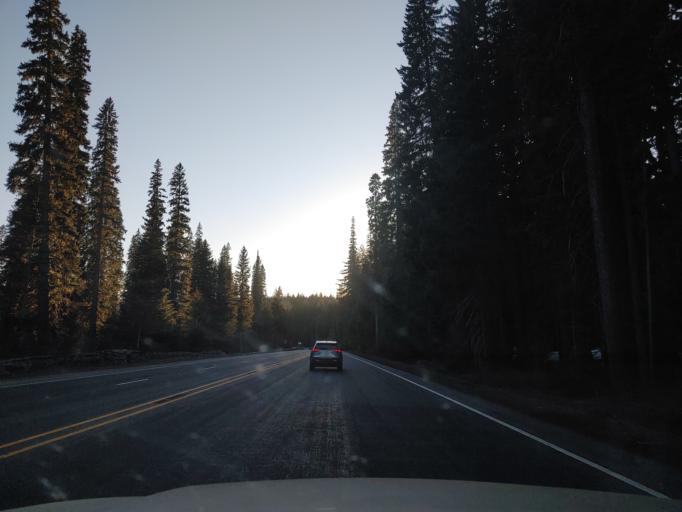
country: US
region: Oregon
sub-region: Lane County
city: Oakridge
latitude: 43.6165
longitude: -122.0954
